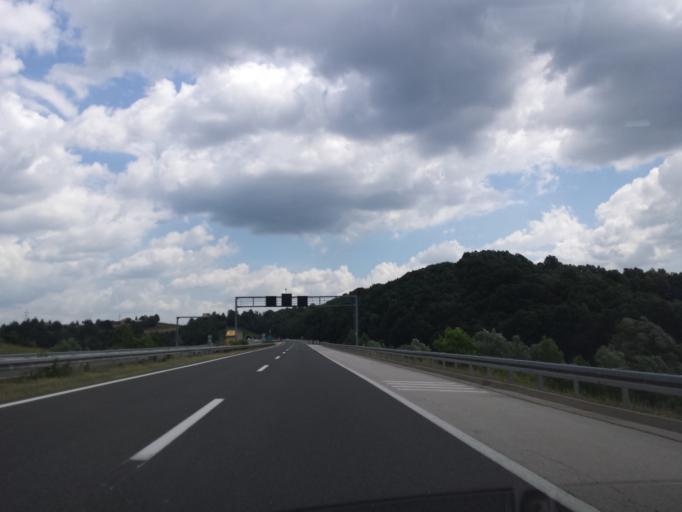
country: HR
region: Karlovacka
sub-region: Grad Karlovac
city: Karlovac
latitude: 45.5016
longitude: 15.4555
